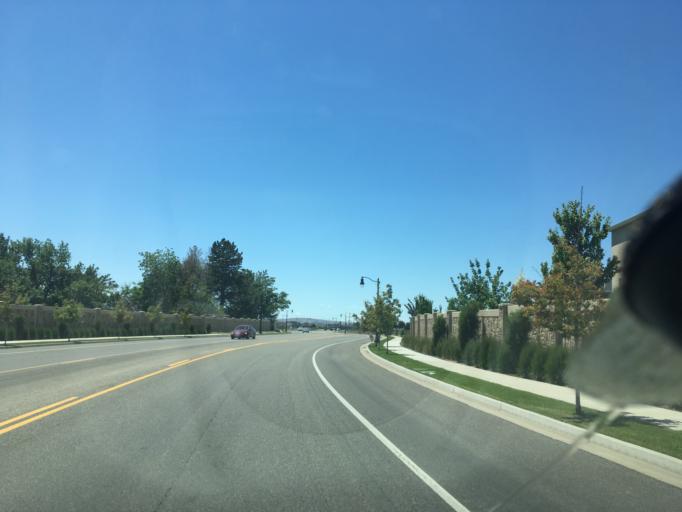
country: US
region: Utah
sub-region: Davis County
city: Layton
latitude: 41.0494
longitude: -111.9802
